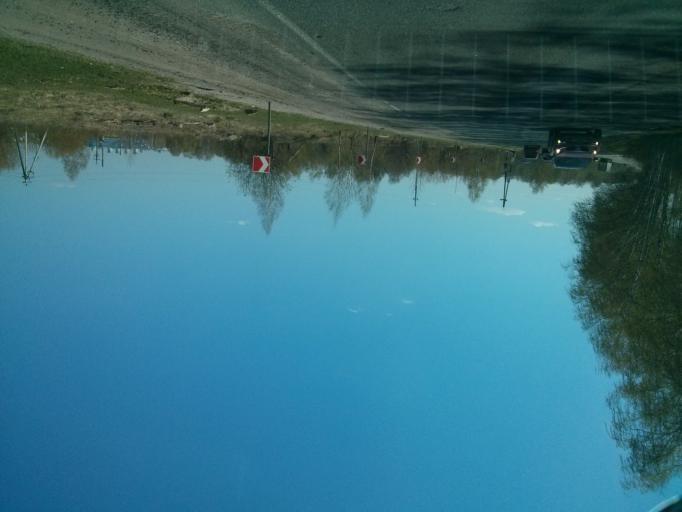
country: RU
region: Nizjnij Novgorod
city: Afonino
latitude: 56.2218
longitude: 44.0570
